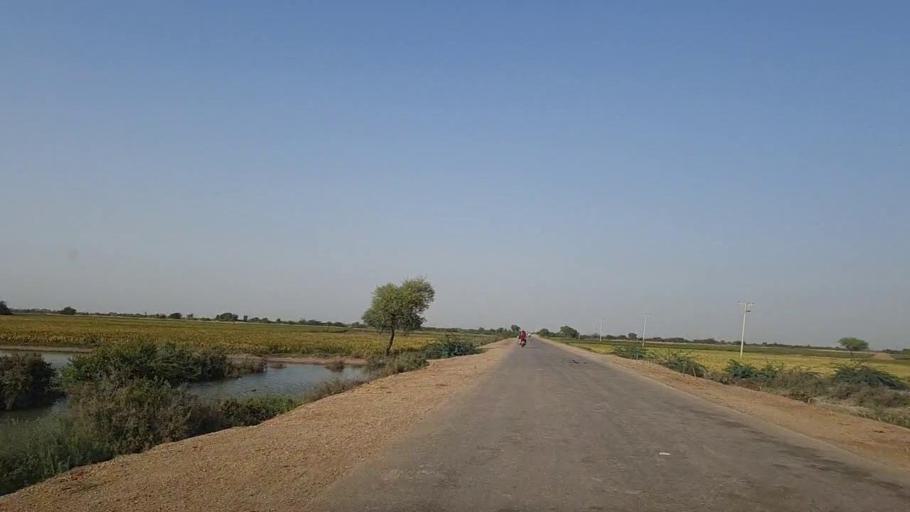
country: PK
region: Sindh
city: Mirpur Batoro
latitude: 24.5957
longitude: 68.3995
